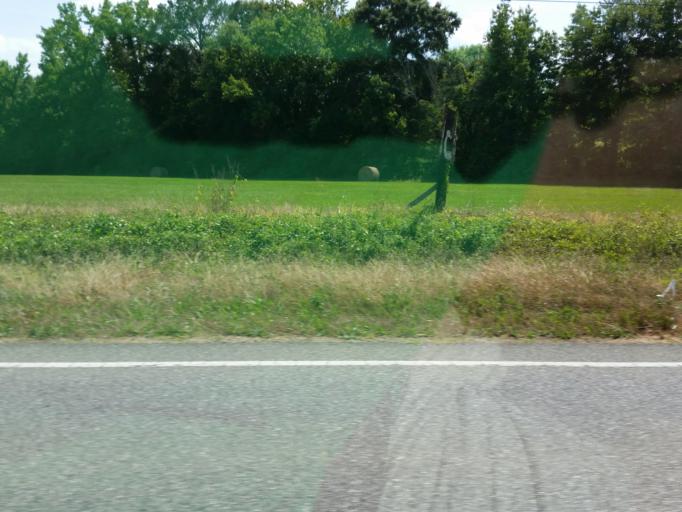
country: US
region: Alabama
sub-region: Marengo County
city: Demopolis
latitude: 32.6345
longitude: -87.8526
